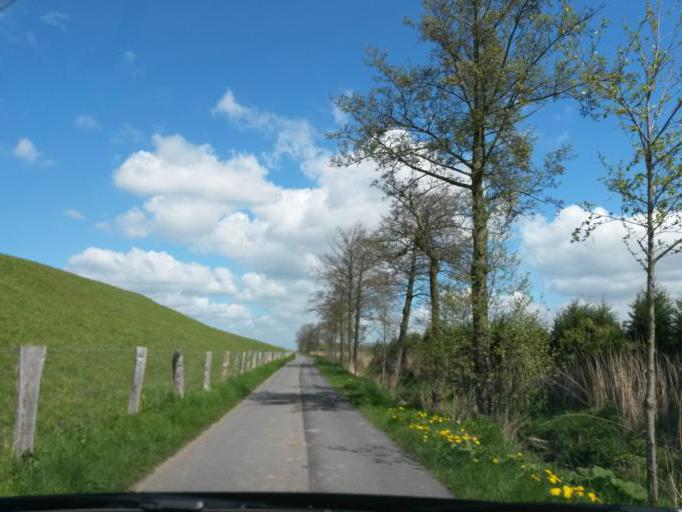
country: DE
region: Schleswig-Holstein
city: Seestermuhe
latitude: 53.6513
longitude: 9.5580
